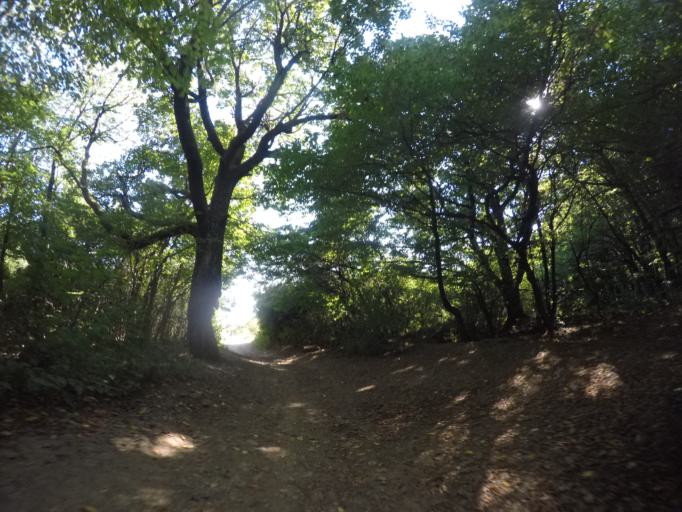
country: SK
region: Kosicky
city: Kosice
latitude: 48.7414
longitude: 21.2087
